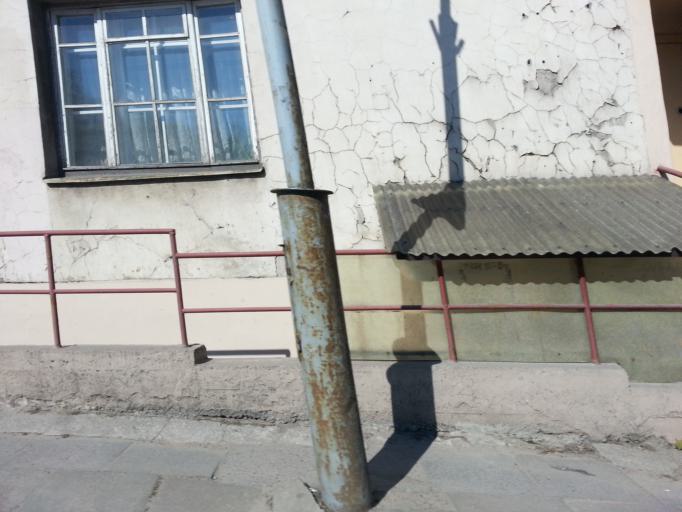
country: LT
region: Vilnius County
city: Rasos
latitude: 54.6920
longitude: 25.3051
